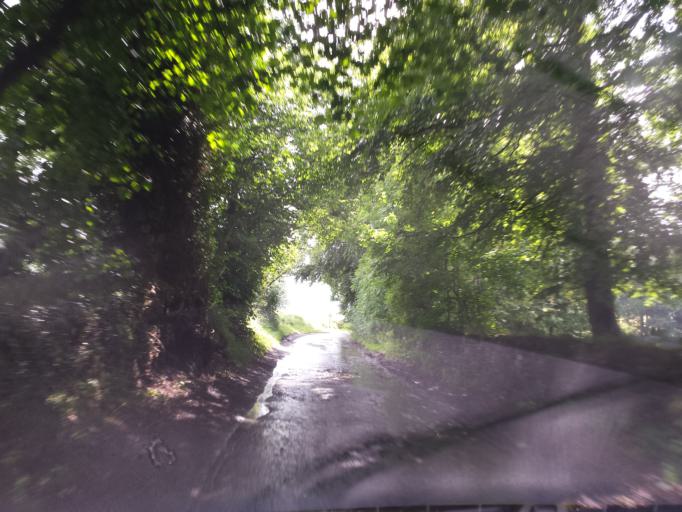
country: GB
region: Scotland
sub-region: The Scottish Borders
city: Saint Boswells
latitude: 55.5925
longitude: -2.6443
